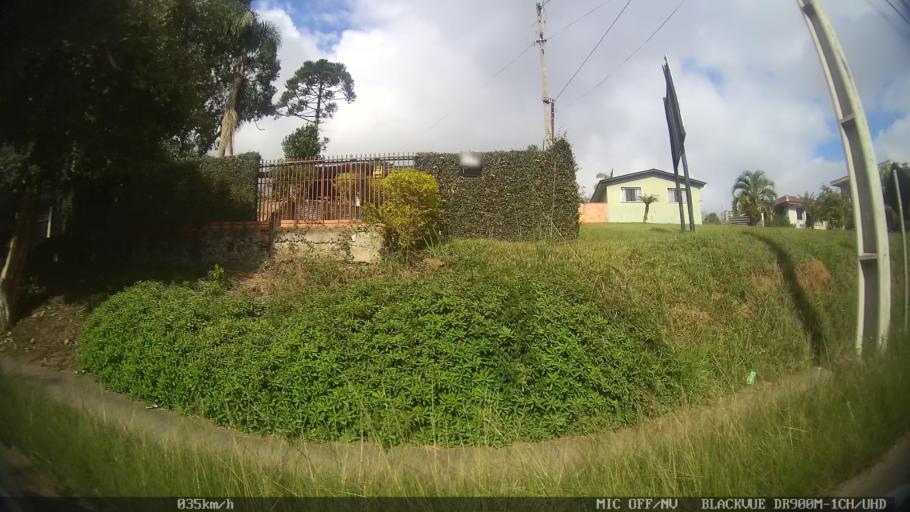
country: BR
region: Parana
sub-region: Curitiba
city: Curitiba
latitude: -25.3607
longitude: -49.2467
